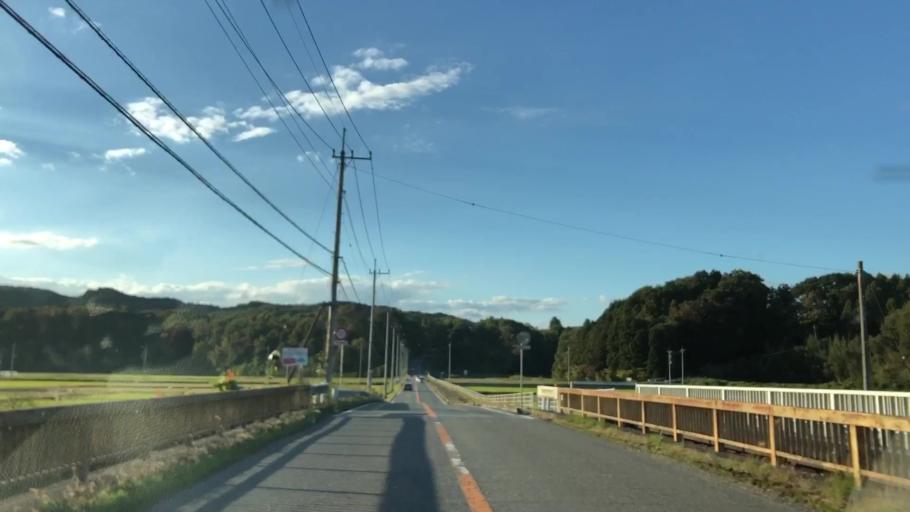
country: JP
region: Ibaraki
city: Tomobe
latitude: 36.4448
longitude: 140.3616
